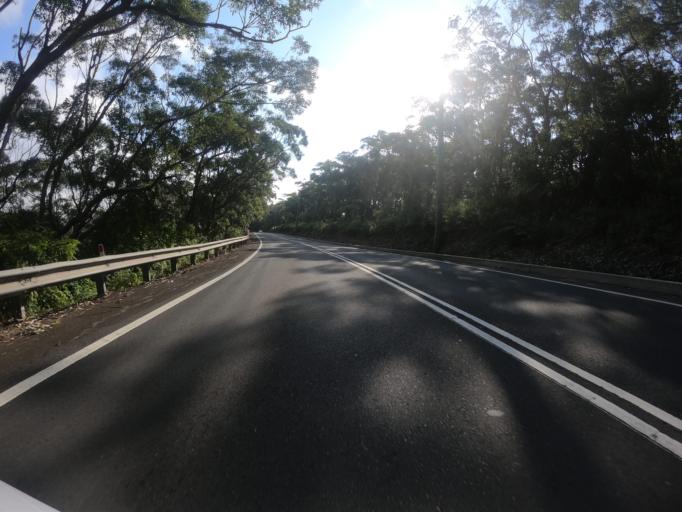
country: AU
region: New South Wales
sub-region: Wollongong
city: Helensburgh
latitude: -34.2214
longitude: 150.9930
